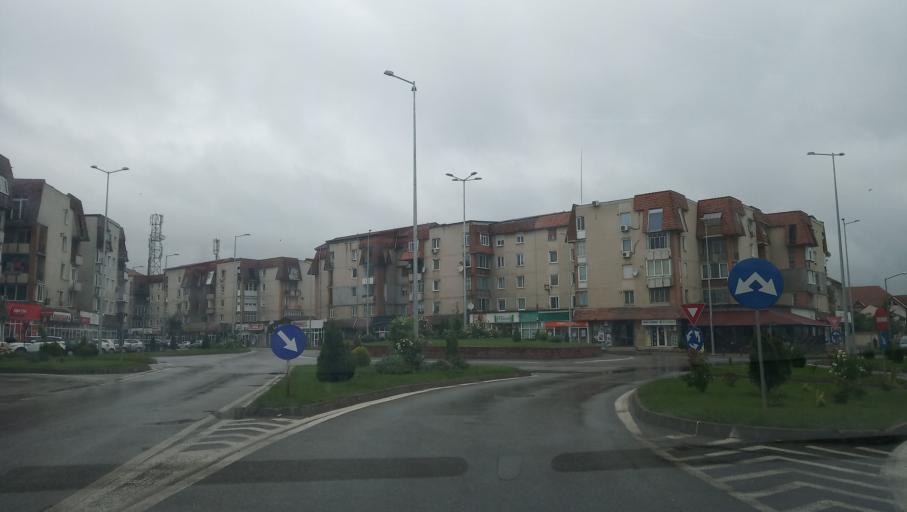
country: RO
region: Alba
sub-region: Municipiul Sebes
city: Sebes
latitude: 45.9551
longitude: 23.5784
